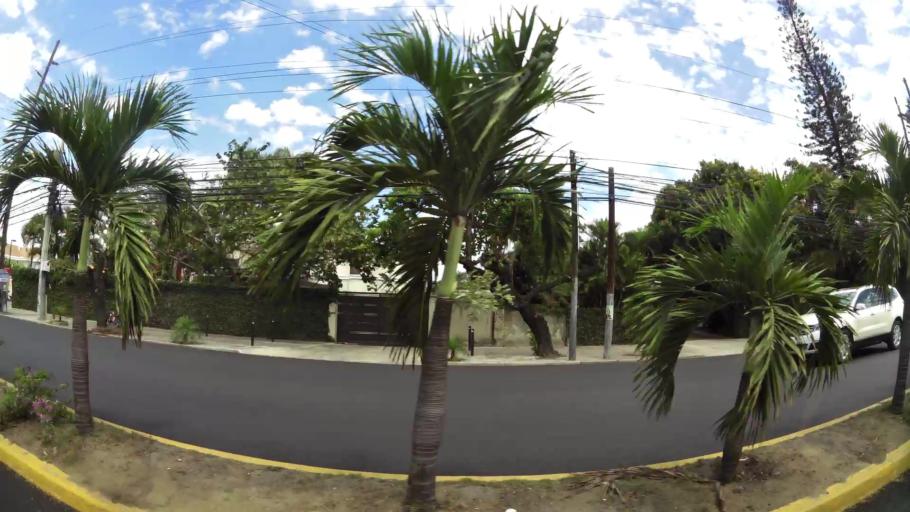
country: DO
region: Santiago
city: Santiago de los Caballeros
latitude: 19.4588
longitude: -70.6780
